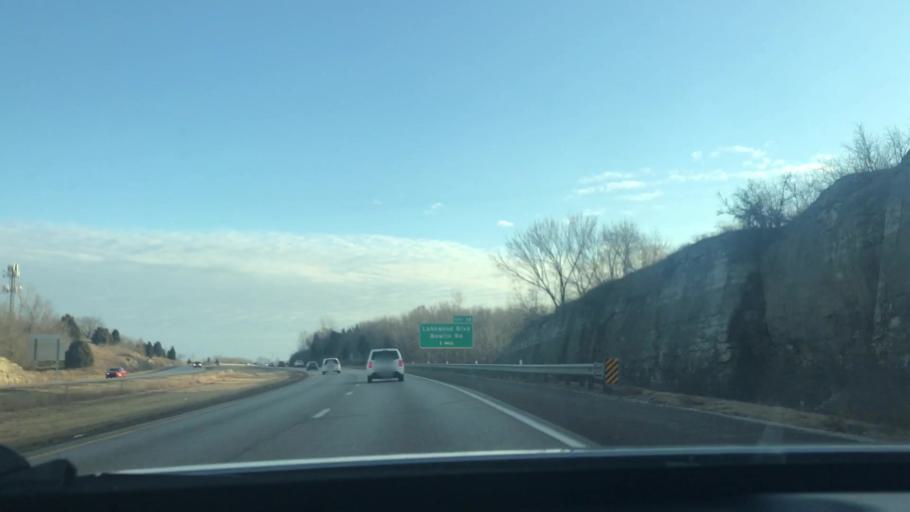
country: US
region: Missouri
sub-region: Jackson County
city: East Independence
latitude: 39.0185
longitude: -94.3595
